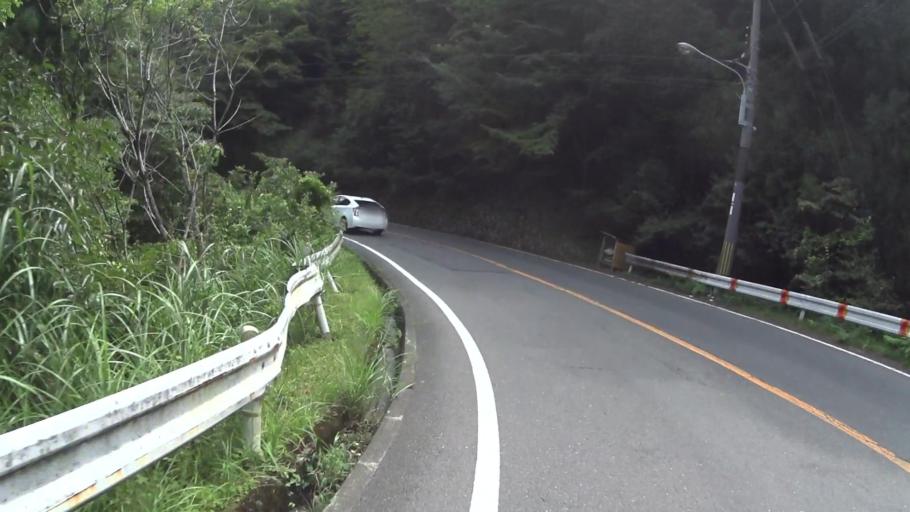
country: JP
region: Kyoto
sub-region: Kyoto-shi
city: Kamigyo-ku
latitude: 35.1089
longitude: 135.8103
